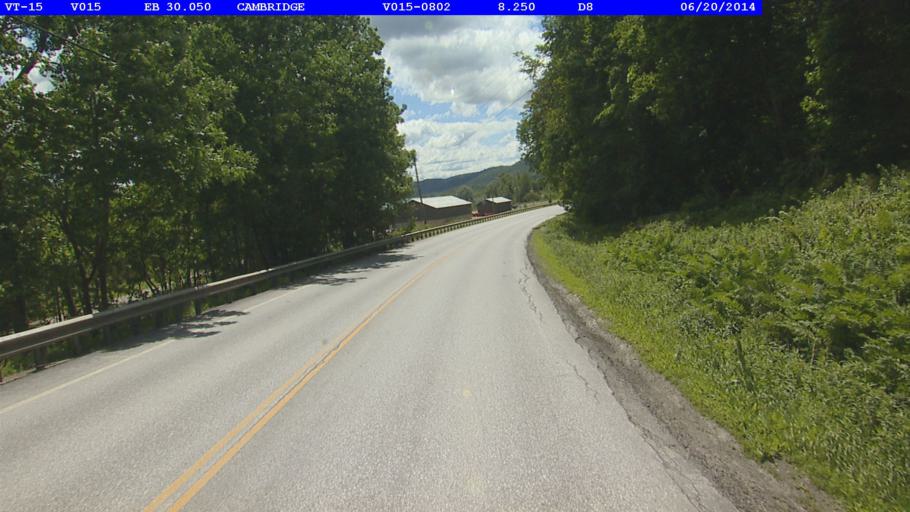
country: US
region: Vermont
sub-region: Lamoille County
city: Johnson
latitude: 44.6655
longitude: -72.7762
